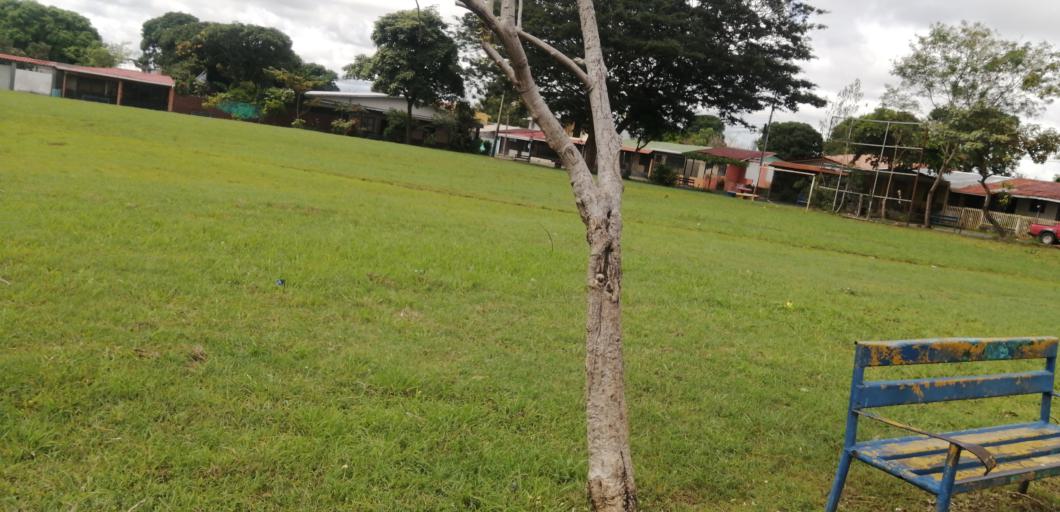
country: CR
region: Guanacaste
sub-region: Canton de Canas
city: Canas
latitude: 10.4320
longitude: -85.0912
